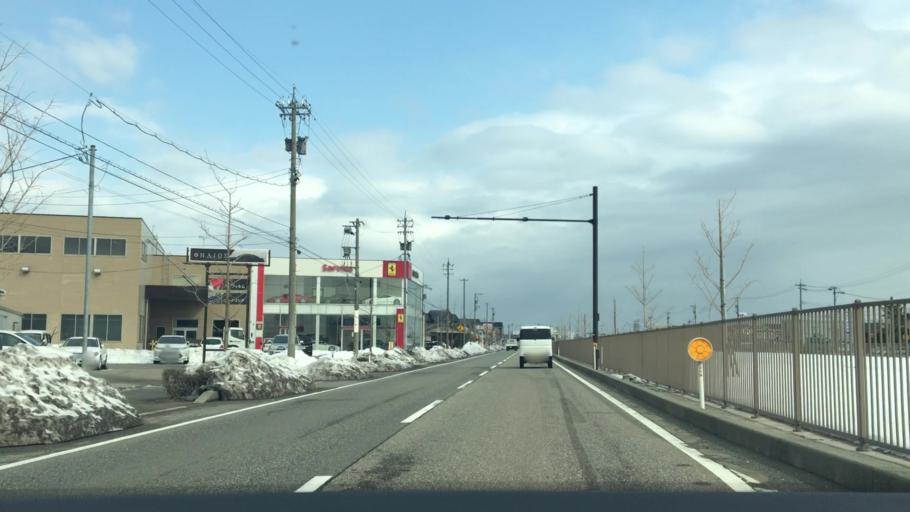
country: JP
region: Ishikawa
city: Nonoichi
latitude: 36.5648
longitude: 136.5805
